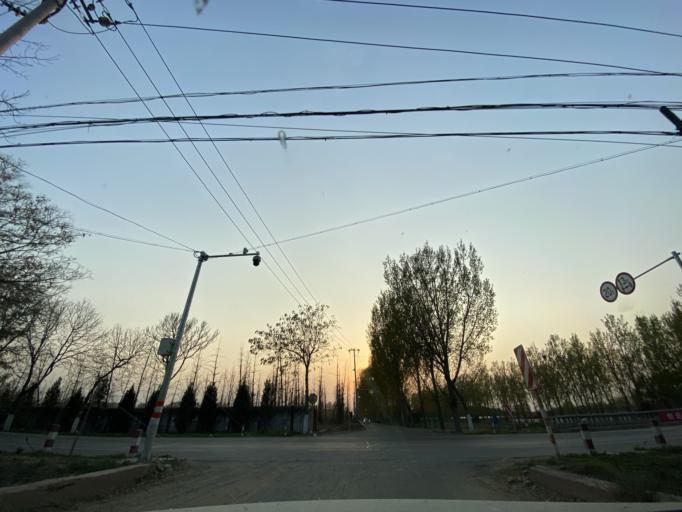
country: CN
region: Beijing
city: Weishanzhuang
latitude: 39.6063
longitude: 116.4098
